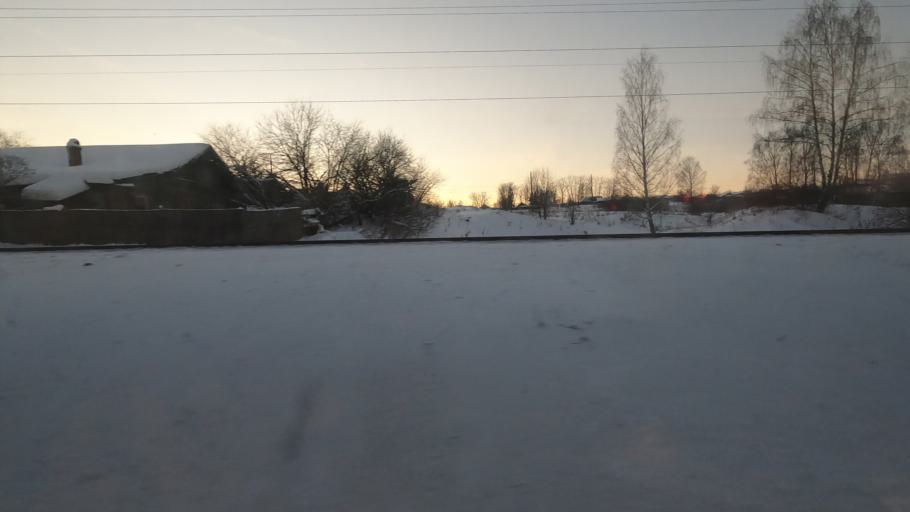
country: RU
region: Moskovskaya
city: Yermolino
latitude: 56.1520
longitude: 37.5033
